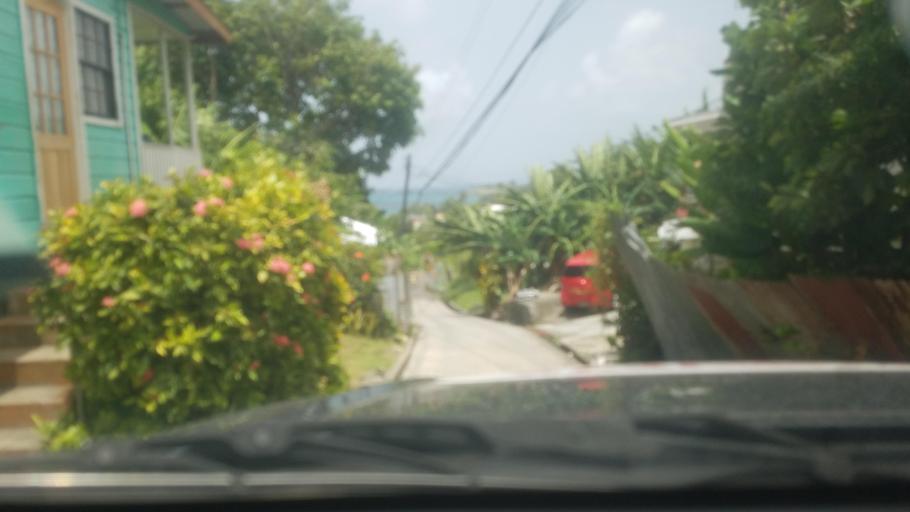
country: LC
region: Laborie Quarter
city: Laborie
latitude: 13.7516
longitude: -60.9923
